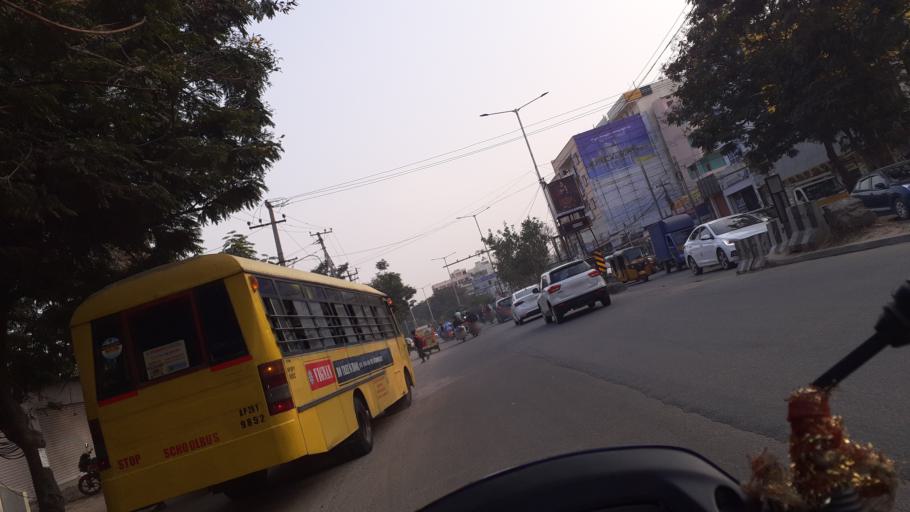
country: IN
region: Telangana
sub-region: Rangareddi
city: Kukatpalli
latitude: 17.4763
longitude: 78.3631
